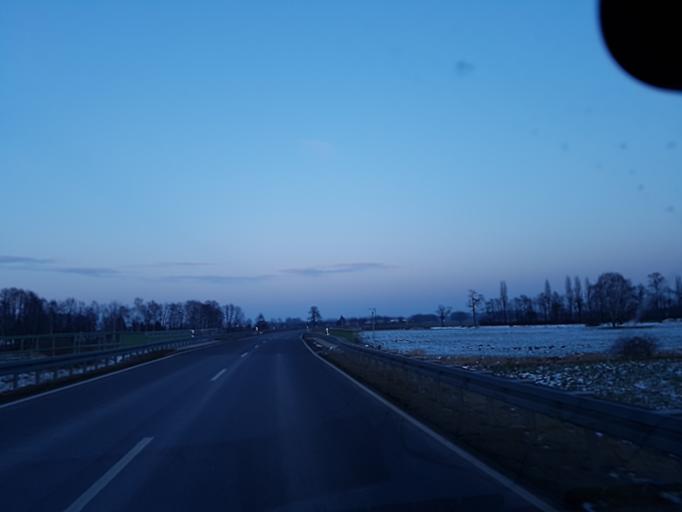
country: DE
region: Brandenburg
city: Bad Liebenwerda
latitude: 51.5073
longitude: 13.3496
